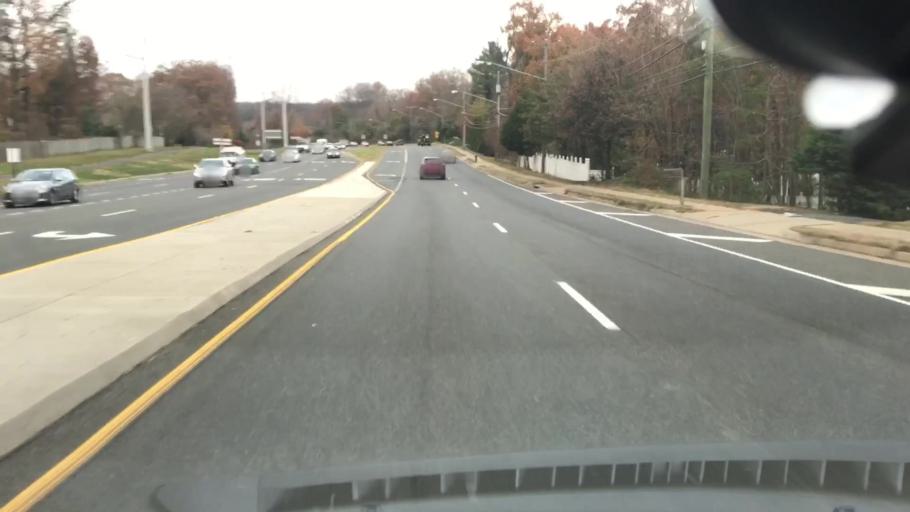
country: US
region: Virginia
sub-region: City of Fairfax
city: Fairfax
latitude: 38.8283
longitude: -77.3179
